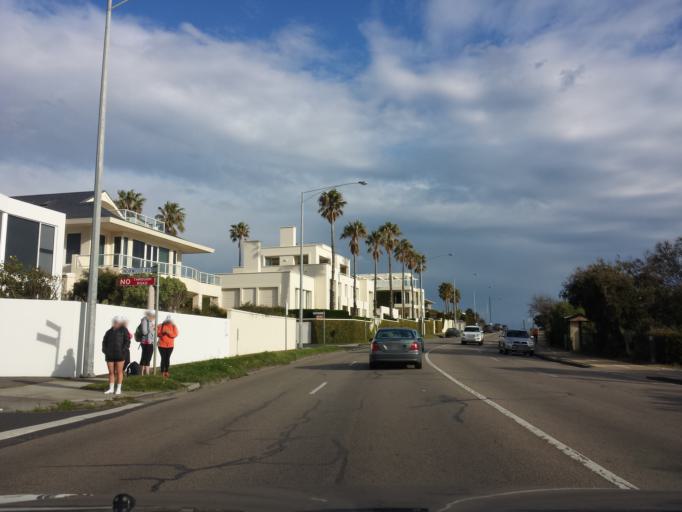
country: AU
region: Victoria
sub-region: Bayside
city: North Brighton
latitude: -37.9201
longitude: 144.9881
